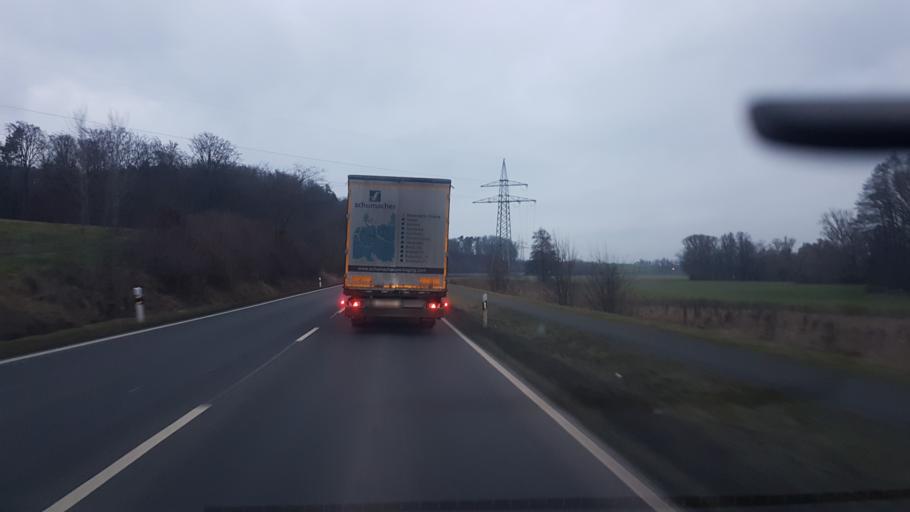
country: DE
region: Bavaria
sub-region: Regierungsbezirk Unterfranken
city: Rentweinsdorf
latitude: 50.0696
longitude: 10.7965
